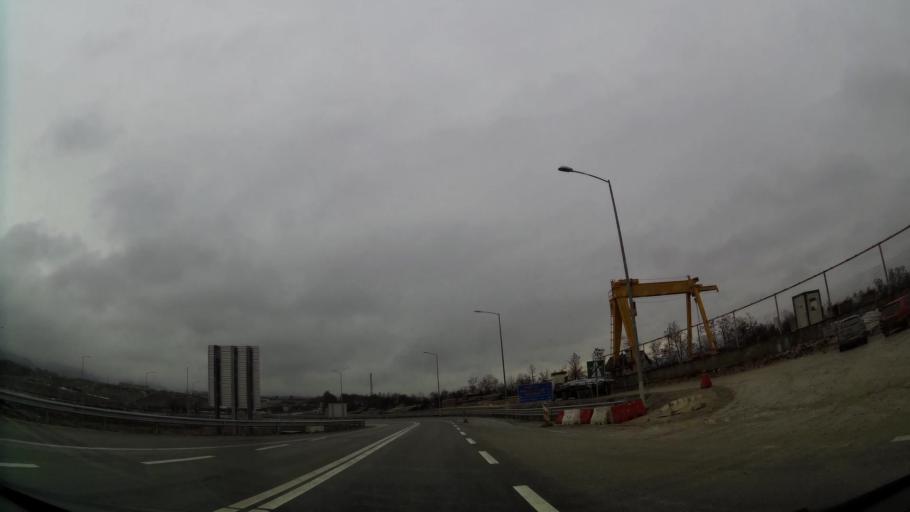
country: XK
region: Ferizaj
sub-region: Komuna e Kacanikut
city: Kacanik
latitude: 42.2747
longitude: 21.2165
